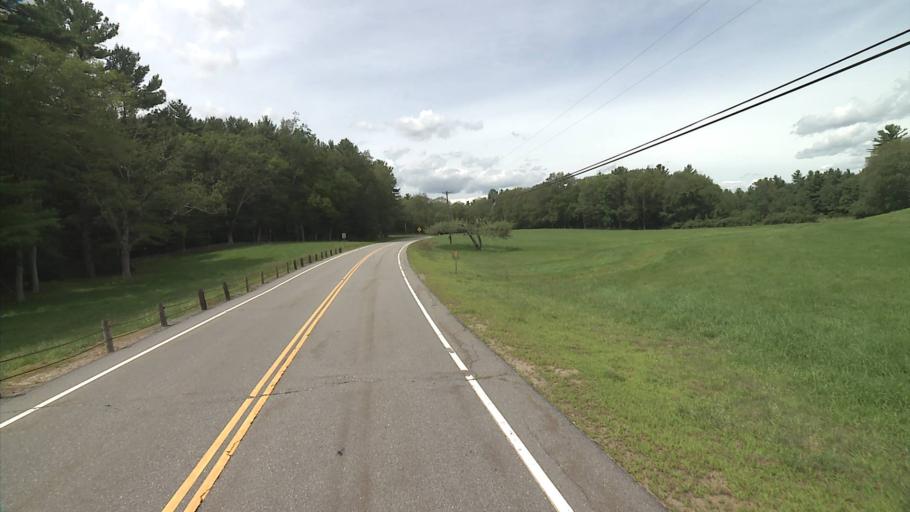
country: US
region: Massachusetts
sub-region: Hampden County
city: Holland
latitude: 41.9400
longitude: -72.1013
